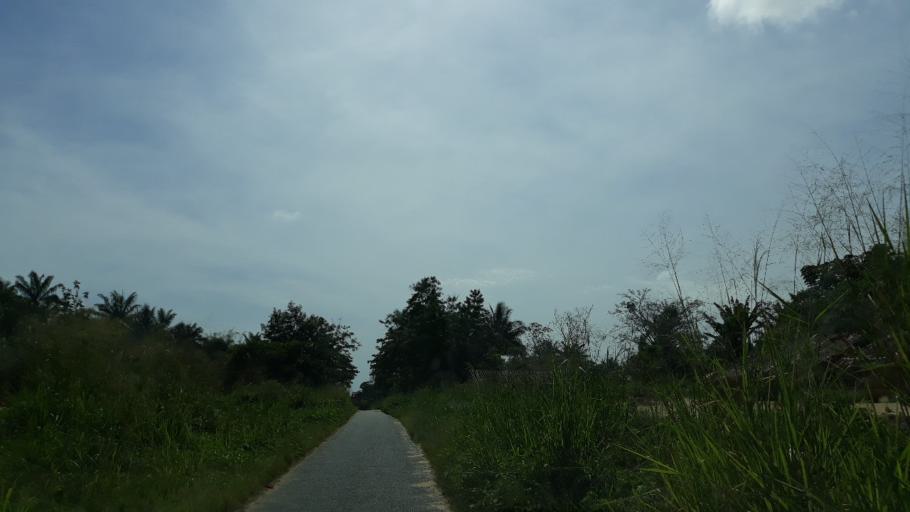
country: CD
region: Maniema
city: Kindu
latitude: -2.9075
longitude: 26.0293
